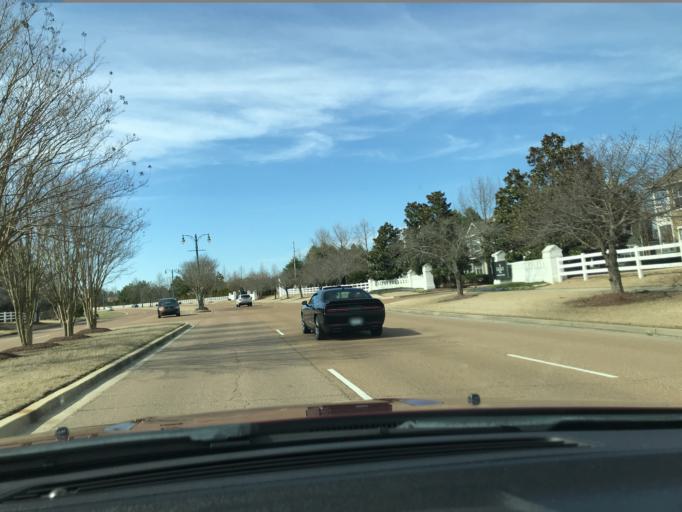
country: US
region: Tennessee
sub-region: Shelby County
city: Collierville
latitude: 35.0397
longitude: -89.7095
